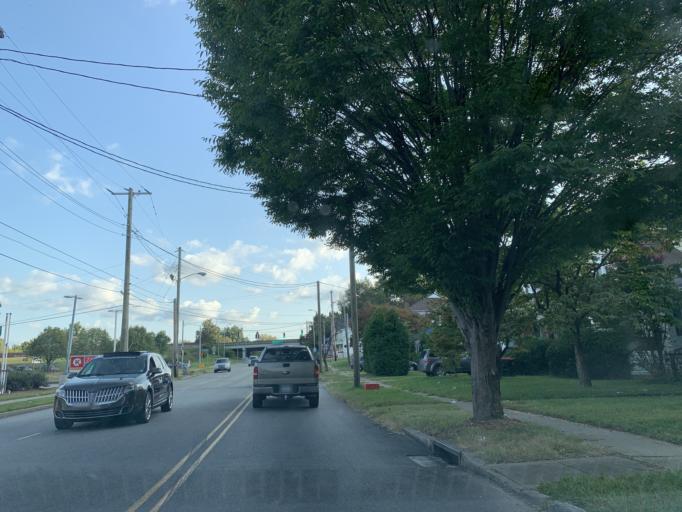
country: US
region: Kentucky
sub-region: Jefferson County
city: Audubon Park
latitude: 38.1922
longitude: -85.7650
